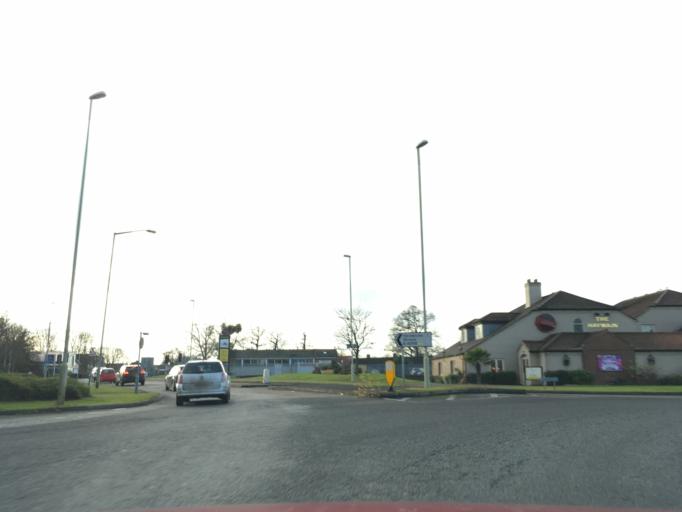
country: GB
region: England
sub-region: Gloucestershire
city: Gloucester
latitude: 51.8274
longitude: -2.2770
